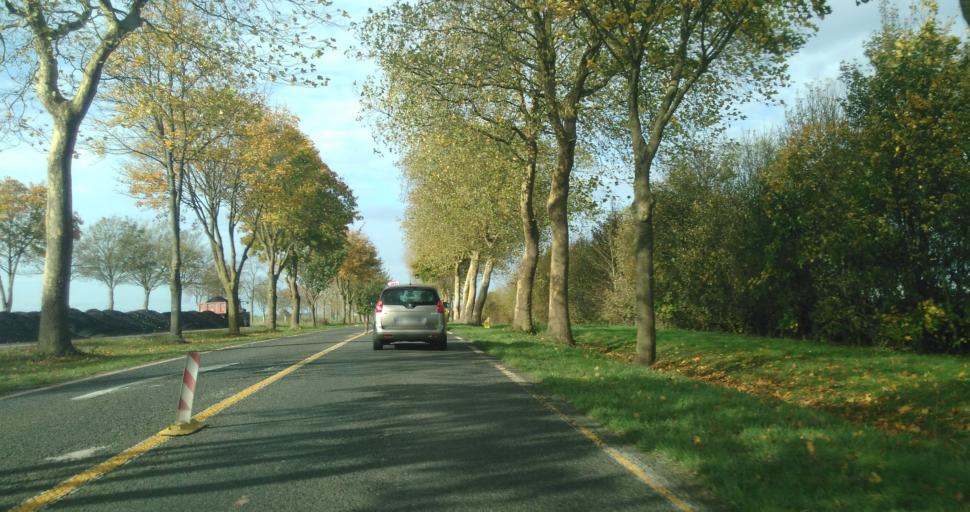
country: FR
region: Nord-Pas-de-Calais
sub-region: Departement du Pas-de-Calais
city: Aubigny-en-Artois
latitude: 50.3440
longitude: 2.5877
